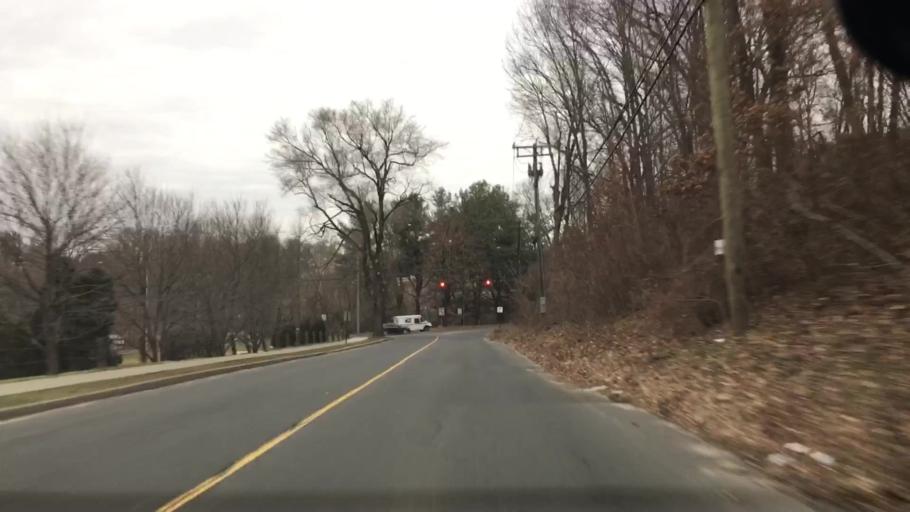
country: US
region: Connecticut
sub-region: Fairfield County
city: Bethel
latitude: 41.4138
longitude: -73.4054
